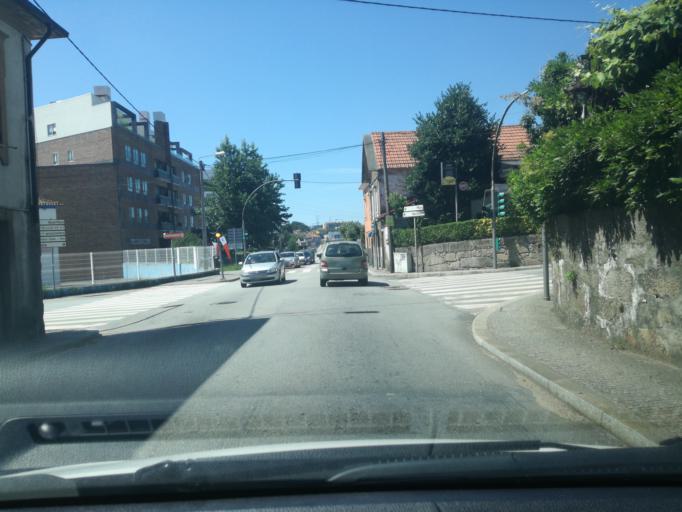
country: PT
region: Porto
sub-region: Maia
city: Nogueira
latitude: 41.2342
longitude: -8.5950
